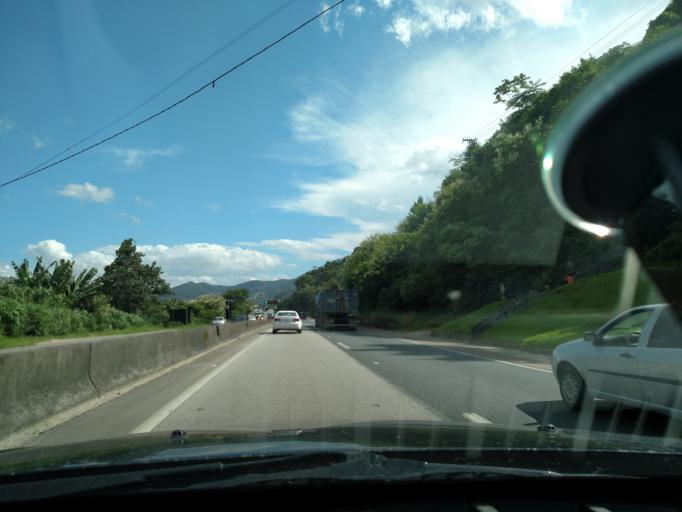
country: BR
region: Santa Catarina
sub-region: Biguacu
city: Biguacu
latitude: -27.4819
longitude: -48.6461
